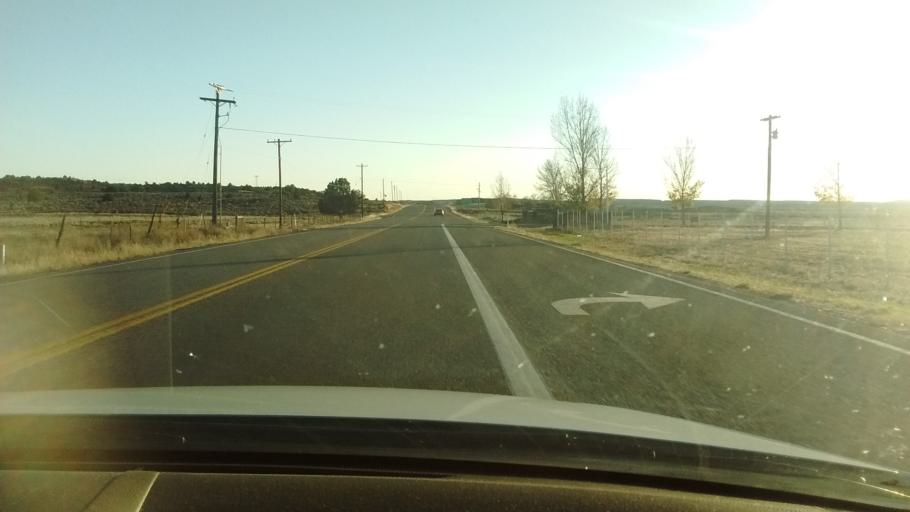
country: US
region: Utah
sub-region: Kane County
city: Kanab
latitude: 37.0100
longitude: -112.5268
